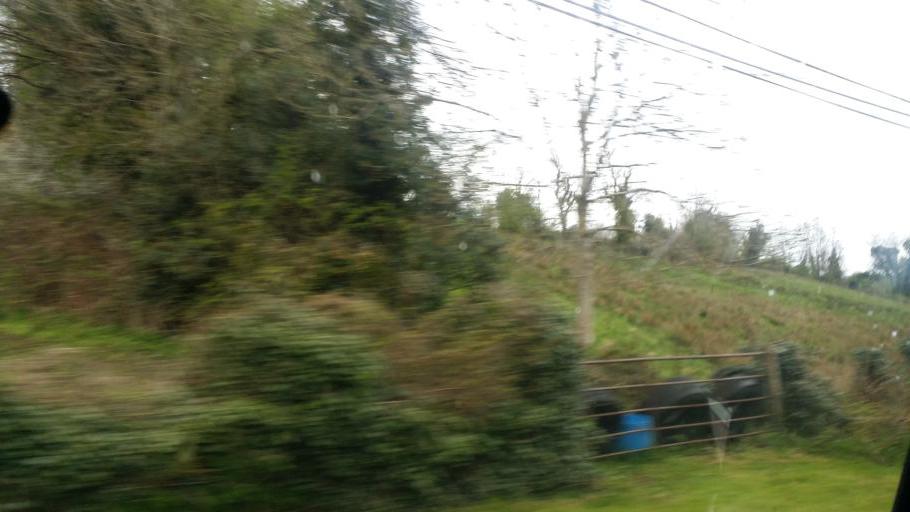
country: IE
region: Ulster
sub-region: An Cabhan
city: Ballyconnell
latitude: 54.1168
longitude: -7.6086
